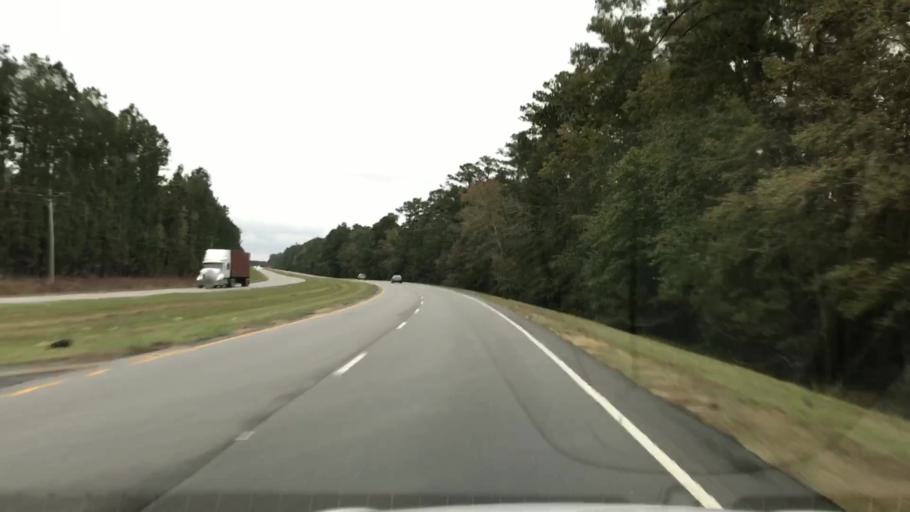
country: US
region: South Carolina
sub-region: Georgetown County
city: Georgetown
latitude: 33.2748
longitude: -79.3526
